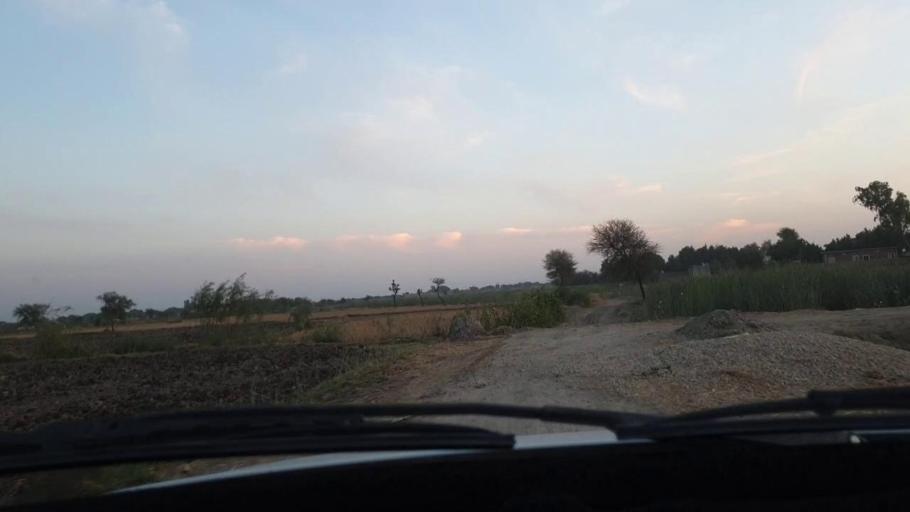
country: PK
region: Sindh
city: Tando Muhammad Khan
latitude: 25.0805
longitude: 68.3989
